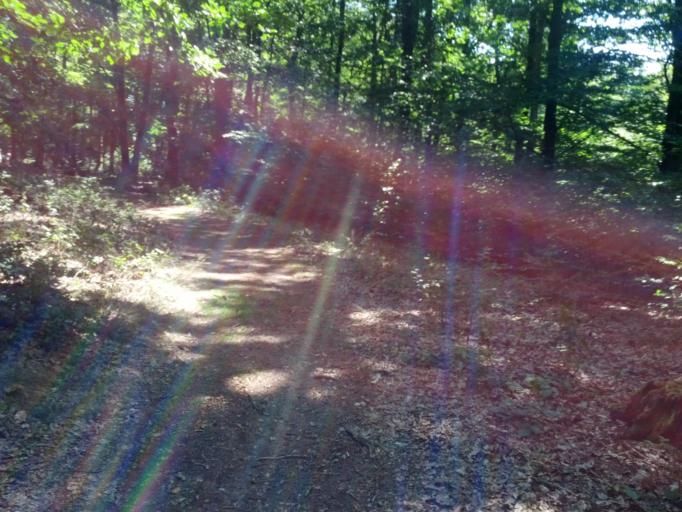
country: DE
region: Thuringia
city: Eisenach
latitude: 50.9582
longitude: 10.3040
